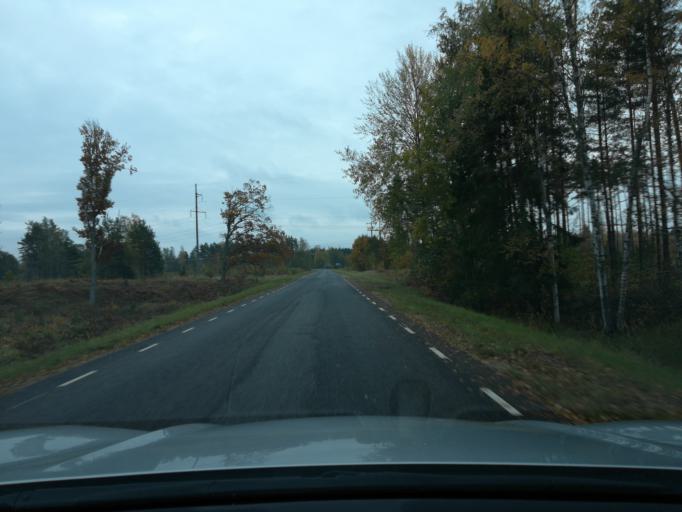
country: EE
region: Ida-Virumaa
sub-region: Johvi vald
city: Johvi
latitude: 59.0191
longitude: 27.4068
